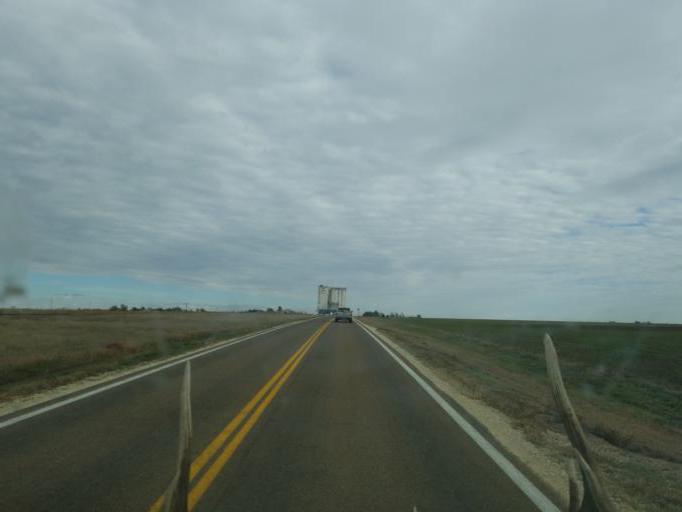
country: US
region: Kansas
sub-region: Logan County
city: Oakley
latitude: 39.0864
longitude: -101.1610
